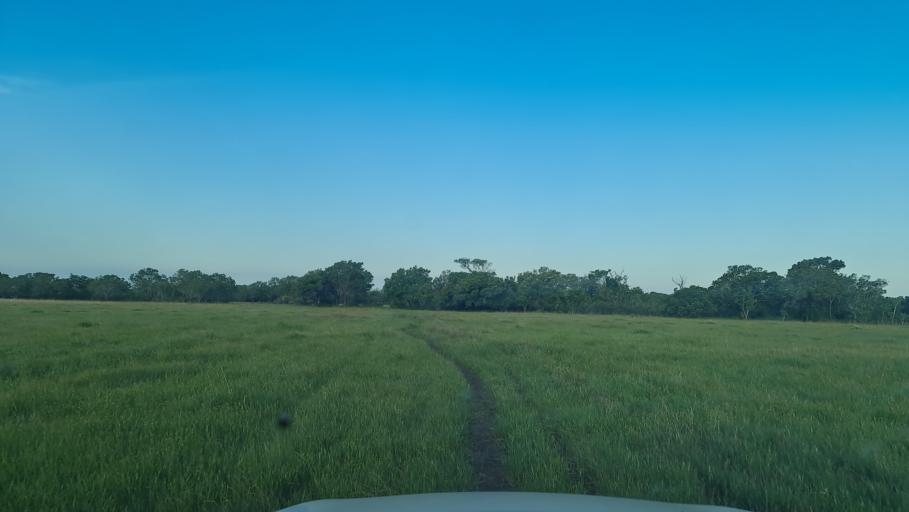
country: MZ
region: Gaza
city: Macia
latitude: -25.2223
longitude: 33.0297
